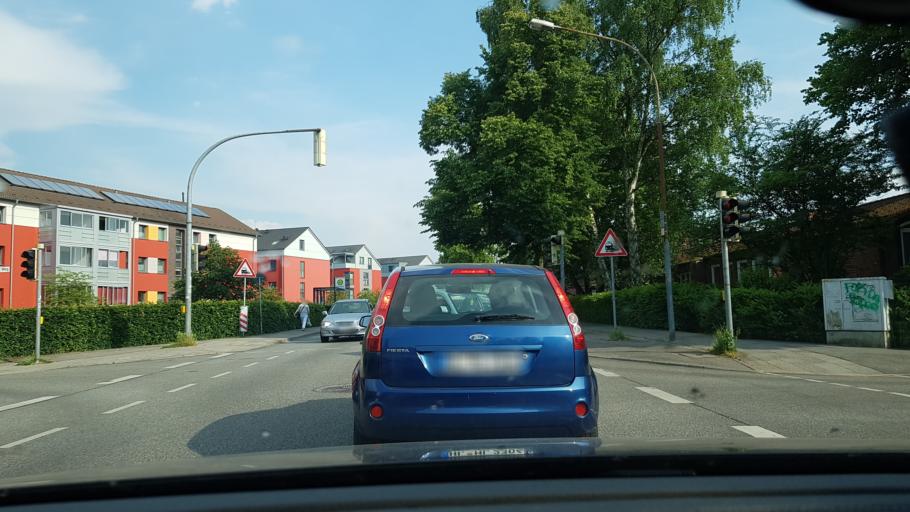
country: DE
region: Schleswig-Holstein
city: Luebeck
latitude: 53.8443
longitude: 10.6998
